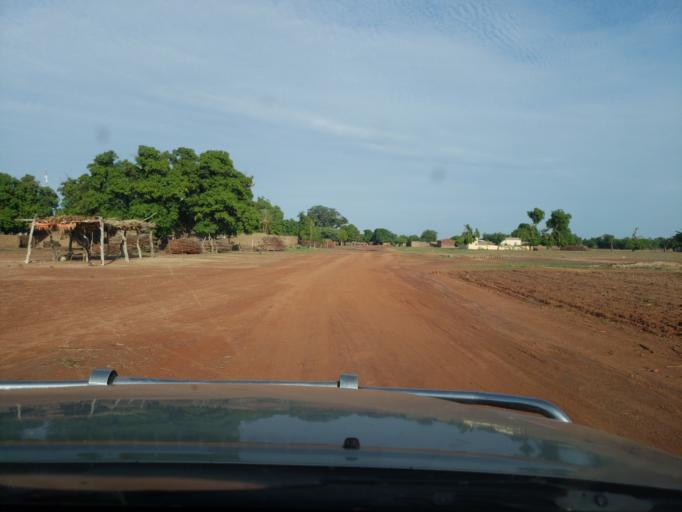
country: ML
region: Sikasso
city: Koutiala
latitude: 12.4228
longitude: -5.6798
